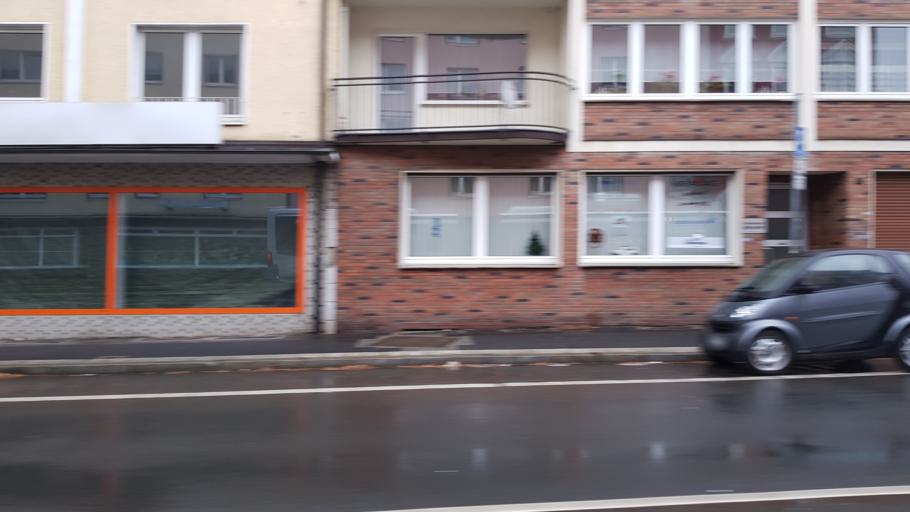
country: DE
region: North Rhine-Westphalia
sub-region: Regierungsbezirk Arnsberg
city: Hagen
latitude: 51.3520
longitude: 7.4798
